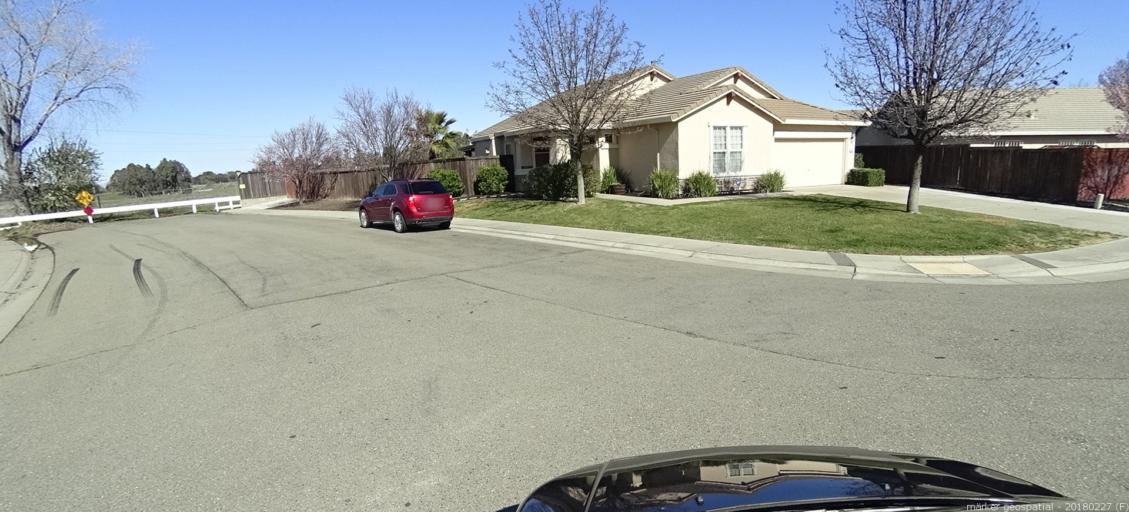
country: US
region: California
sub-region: Sacramento County
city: North Highlands
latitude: 38.7274
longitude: -121.3818
